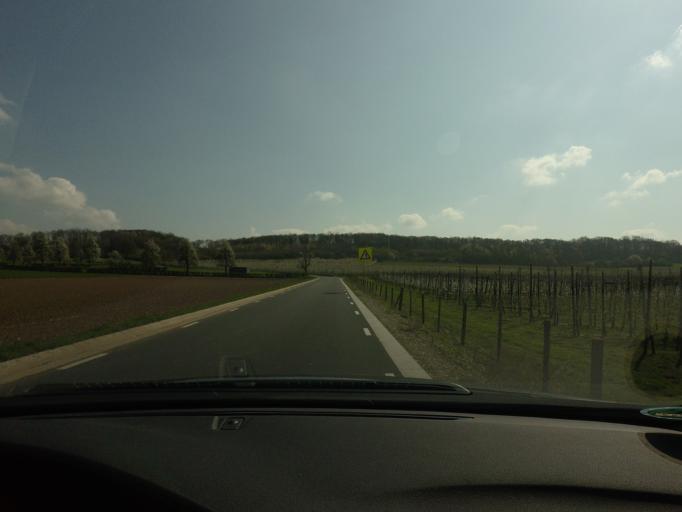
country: NL
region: Limburg
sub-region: Gemeente Maastricht
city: Heer
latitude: 50.8253
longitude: 5.7402
